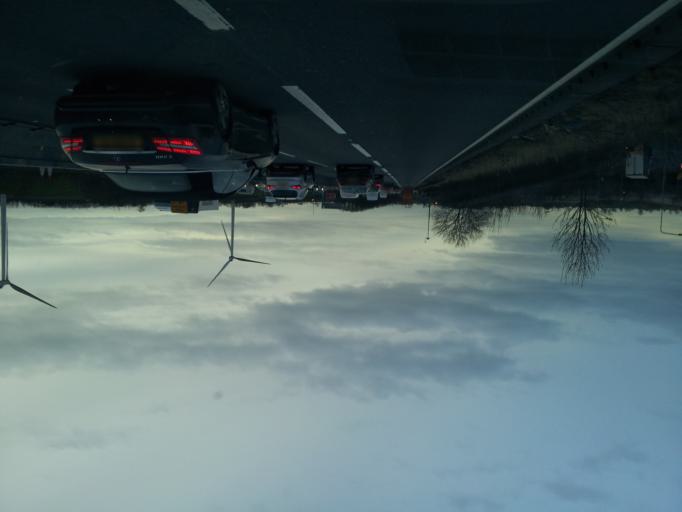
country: GB
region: England
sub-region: Northamptonshire
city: Long Buckby
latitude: 52.3521
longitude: -1.1545
